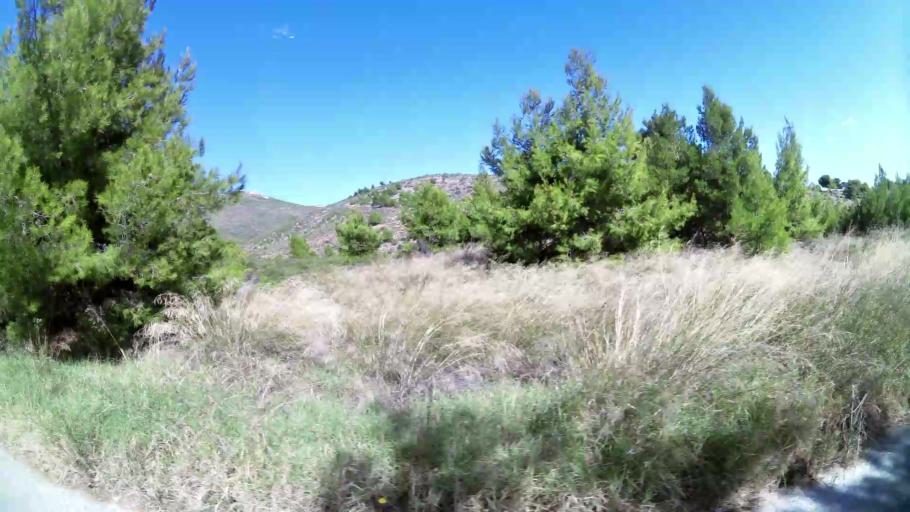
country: GR
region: Attica
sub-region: Nomarchia Anatolikis Attikis
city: Dioni
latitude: 38.0385
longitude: 23.9353
